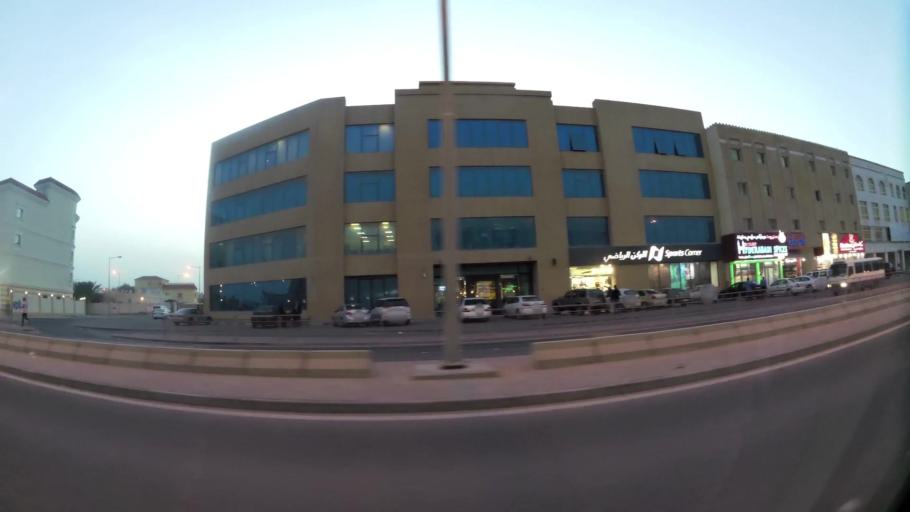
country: QA
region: Al Wakrah
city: Al Wakrah
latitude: 25.1684
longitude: 51.5980
